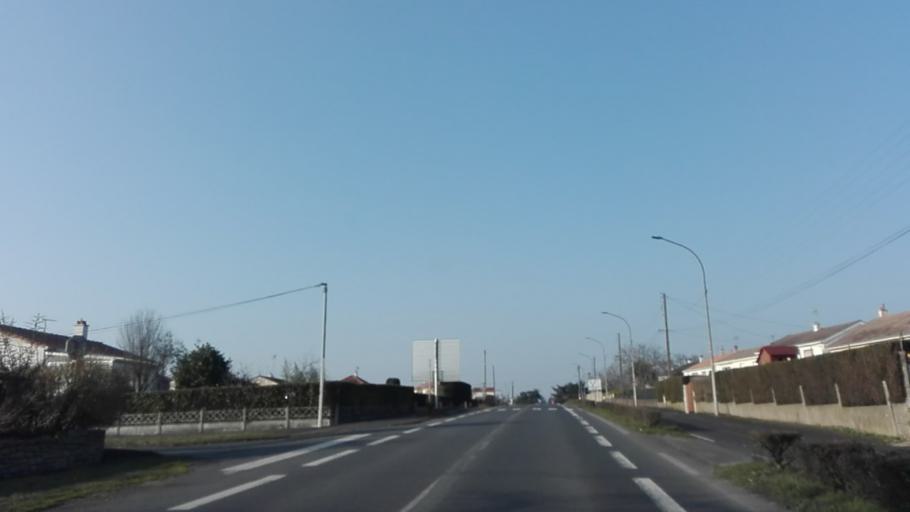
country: FR
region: Pays de la Loire
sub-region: Departement de la Vendee
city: Montaigu
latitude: 46.9664
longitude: -1.3077
